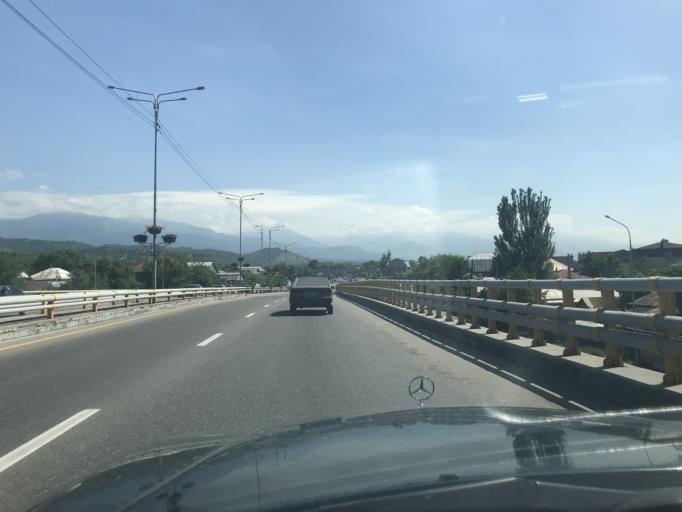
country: KZ
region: Almaty Qalasy
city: Almaty
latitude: 43.2834
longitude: 76.9867
